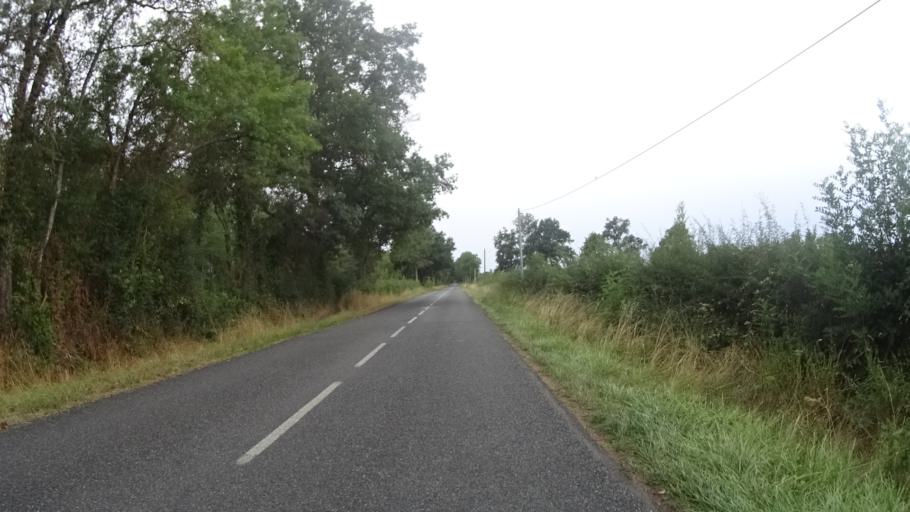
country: FR
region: Bourgogne
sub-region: Departement de la Nievre
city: Decize
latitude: 46.7924
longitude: 3.5102
